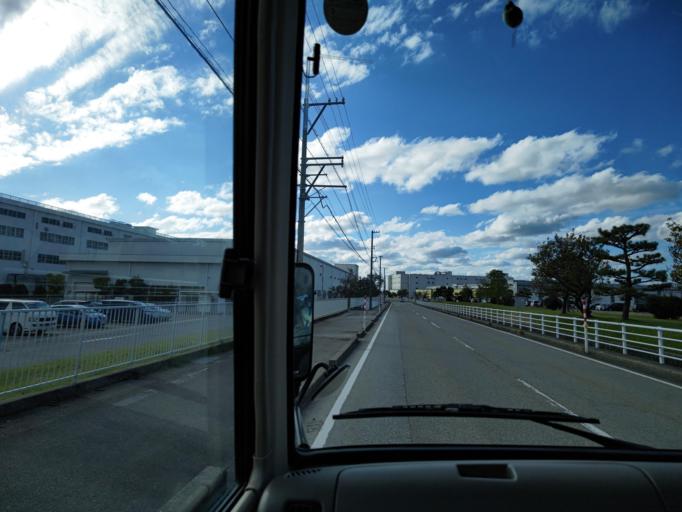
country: JP
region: Toyama
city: Nyuzen
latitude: 36.8927
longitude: 137.4382
